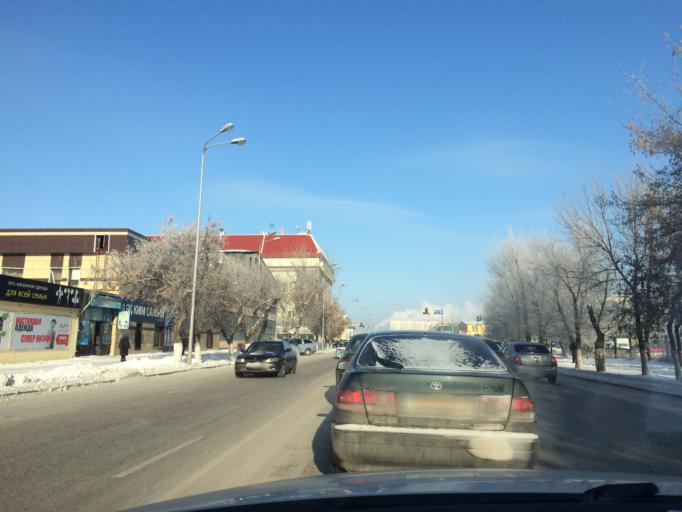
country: KZ
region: Astana Qalasy
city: Astana
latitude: 51.1719
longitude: 71.4385
